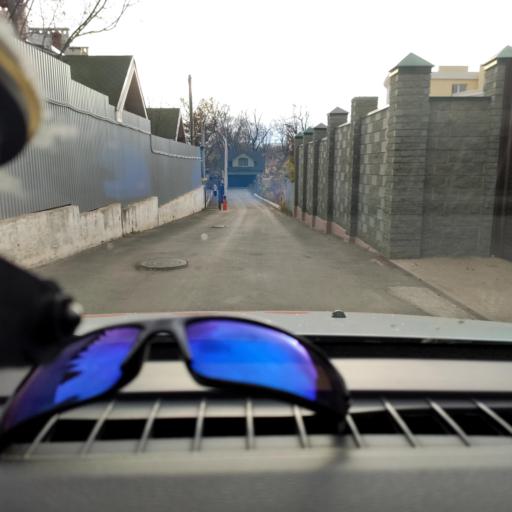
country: RU
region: Samara
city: Samara
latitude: 53.2368
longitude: 50.1736
